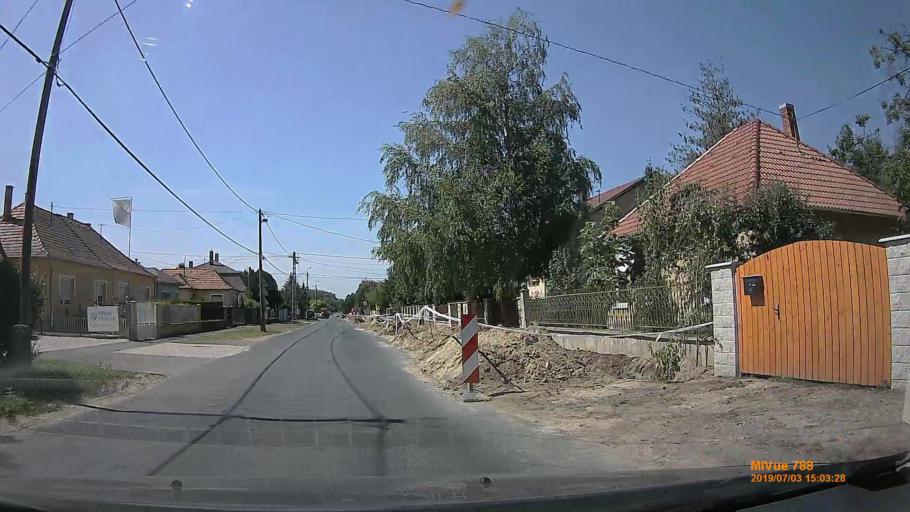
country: HU
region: Gyor-Moson-Sopron
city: Gyorujbarat
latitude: 47.6352
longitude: 17.6082
